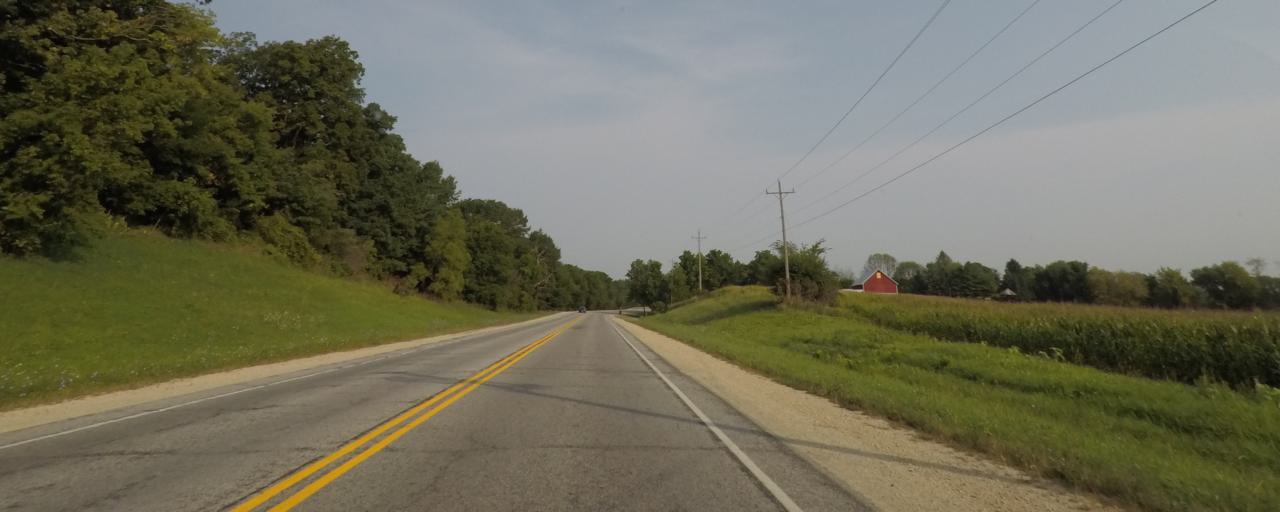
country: US
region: Wisconsin
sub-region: Dane County
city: Deerfield
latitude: 43.0864
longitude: -89.0774
